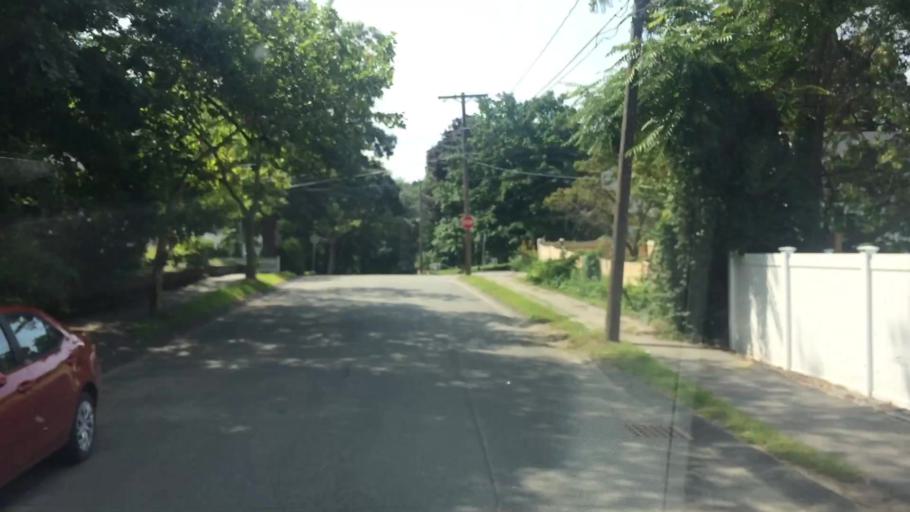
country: US
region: Massachusetts
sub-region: Norfolk County
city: Dedham
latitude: 42.2486
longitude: -71.1478
